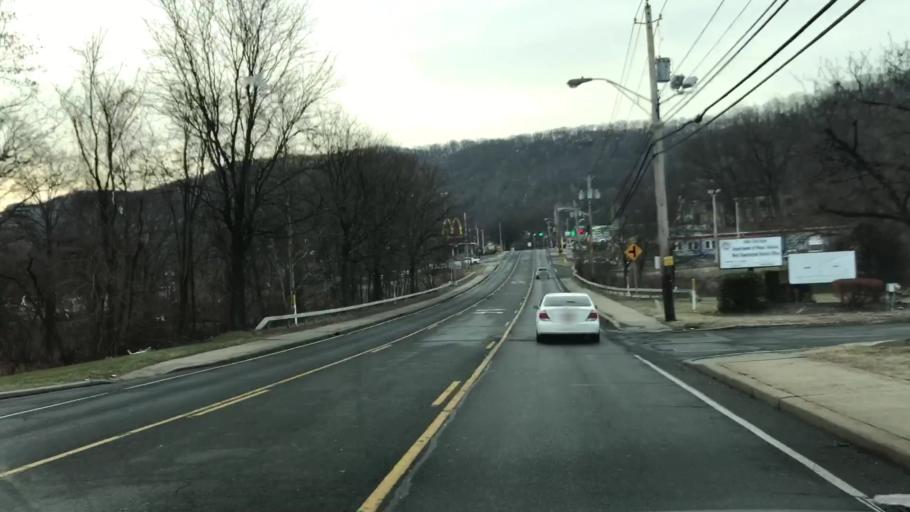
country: US
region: New York
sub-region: Rockland County
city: West Haverstraw
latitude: 41.2052
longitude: -73.9843
